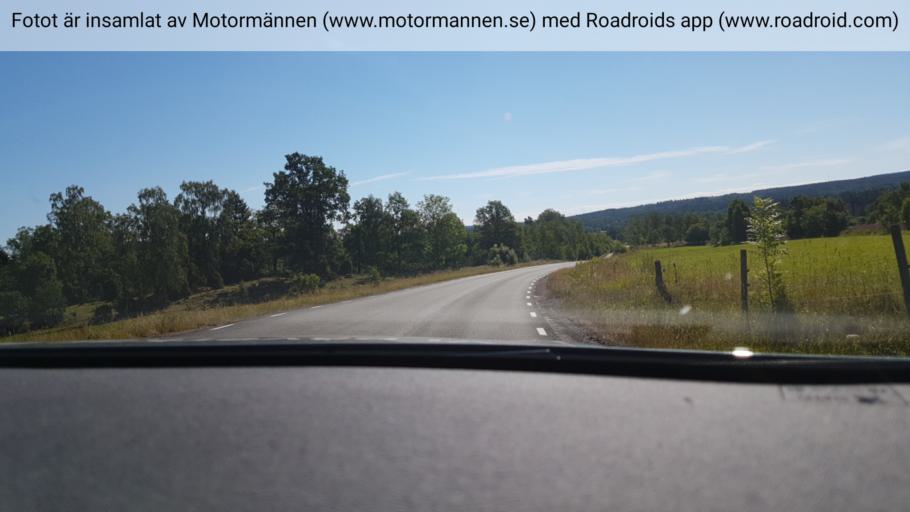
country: SE
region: Vaestra Goetaland
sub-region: Tidaholms Kommun
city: Tidaholm
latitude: 58.1430
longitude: 13.9909
